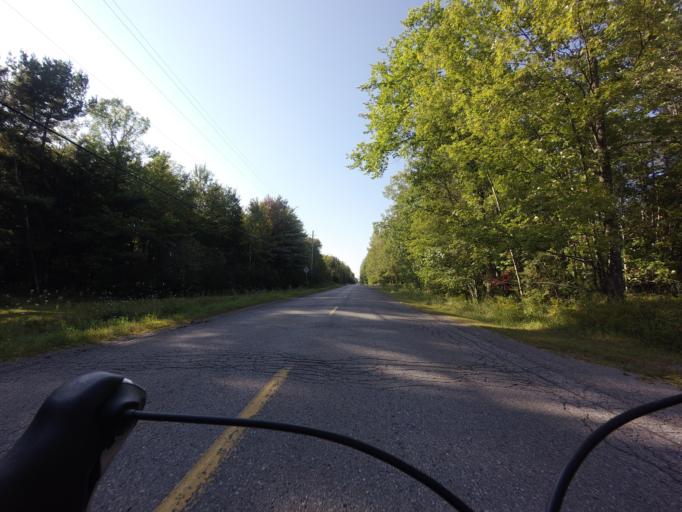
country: CA
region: Ontario
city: Bells Corners
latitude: 45.4707
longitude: -76.0327
